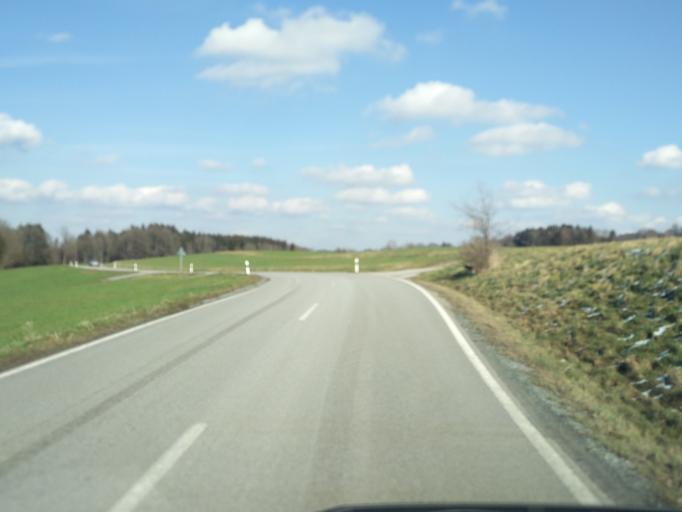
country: DE
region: Bavaria
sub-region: Upper Bavaria
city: Amerang
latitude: 47.9791
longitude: 12.2972
